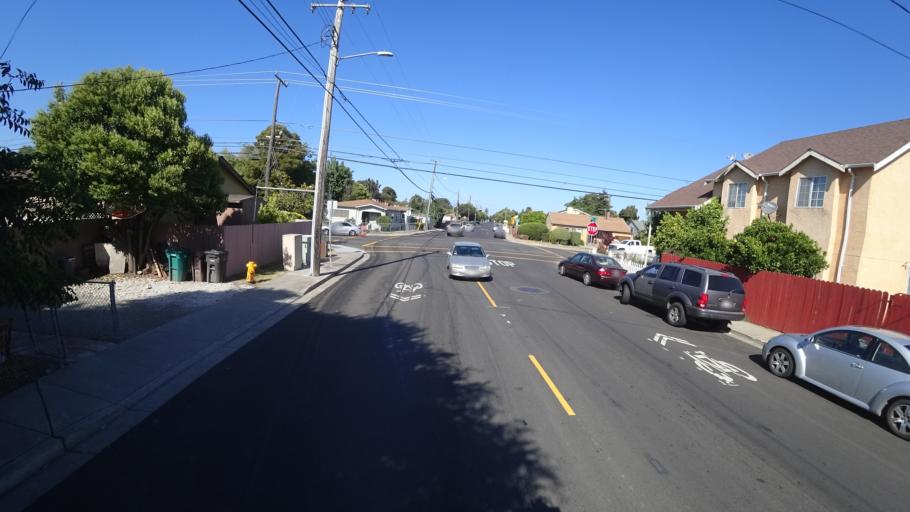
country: US
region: California
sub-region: Alameda County
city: Hayward
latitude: 37.6255
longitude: -122.0656
